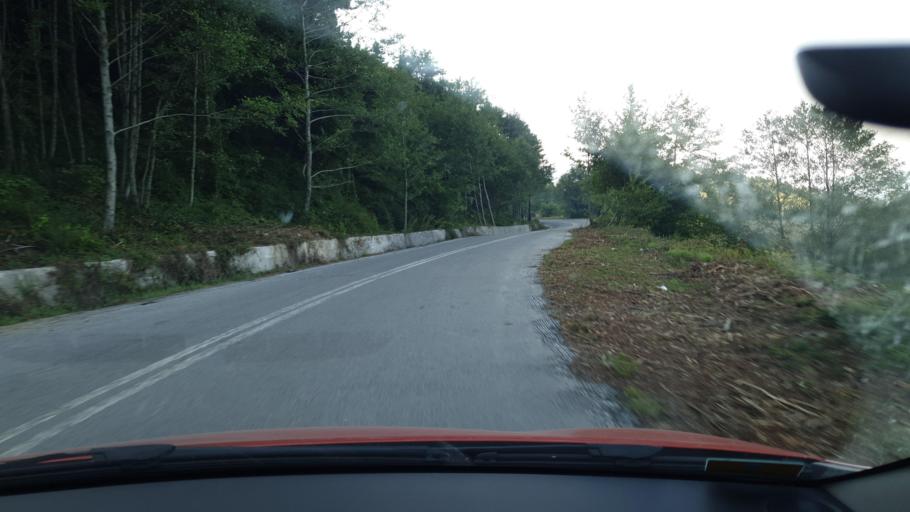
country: GR
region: Central Greece
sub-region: Nomos Evvoias
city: Yimnon
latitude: 38.5949
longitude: 23.8782
